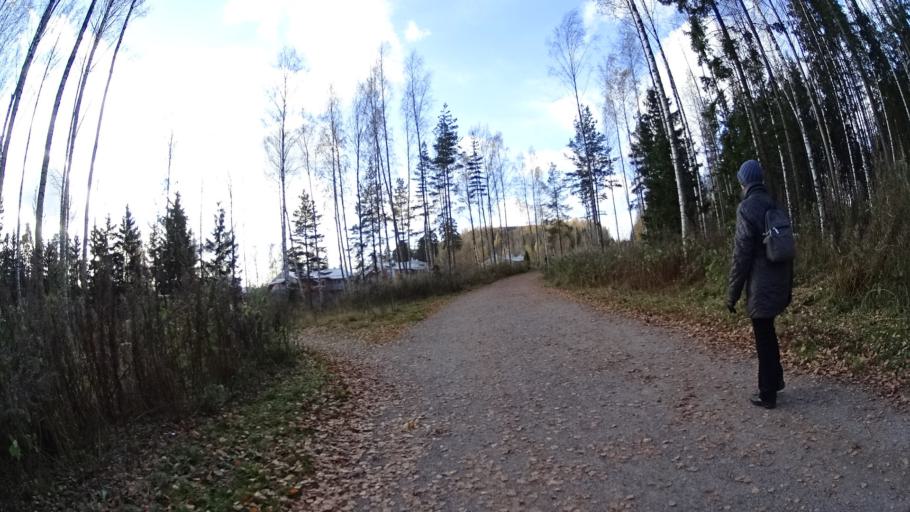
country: FI
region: Uusimaa
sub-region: Helsinki
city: Teekkarikylae
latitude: 60.2552
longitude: 24.8498
